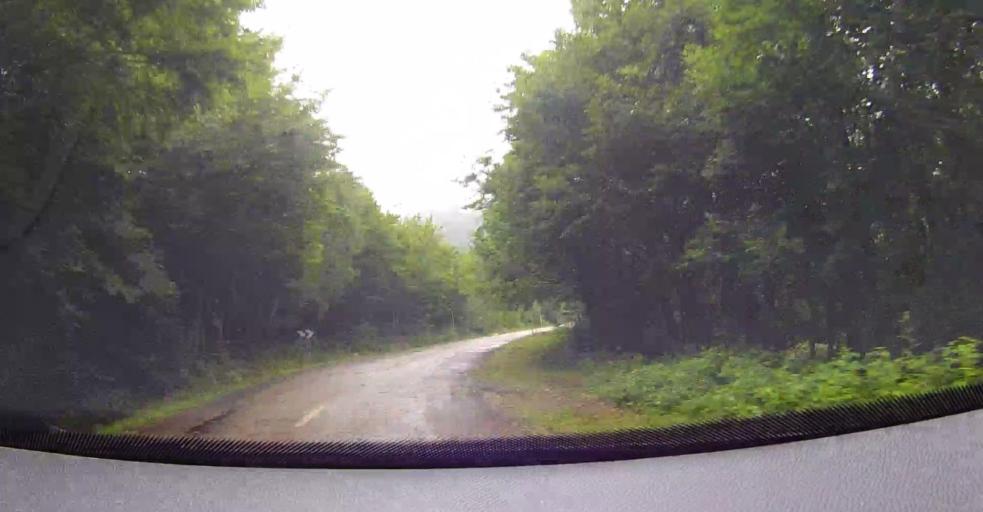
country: ES
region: Castille and Leon
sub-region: Provincia de Leon
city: Puebla de Lillo
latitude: 43.0640
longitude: -5.2697
